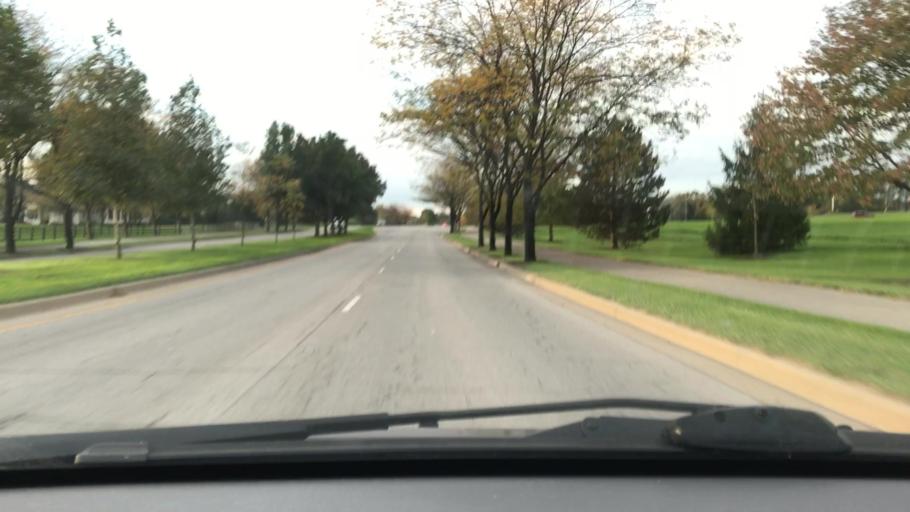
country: US
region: Indiana
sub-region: Hamilton County
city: Carmel
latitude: 39.9761
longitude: -86.0706
